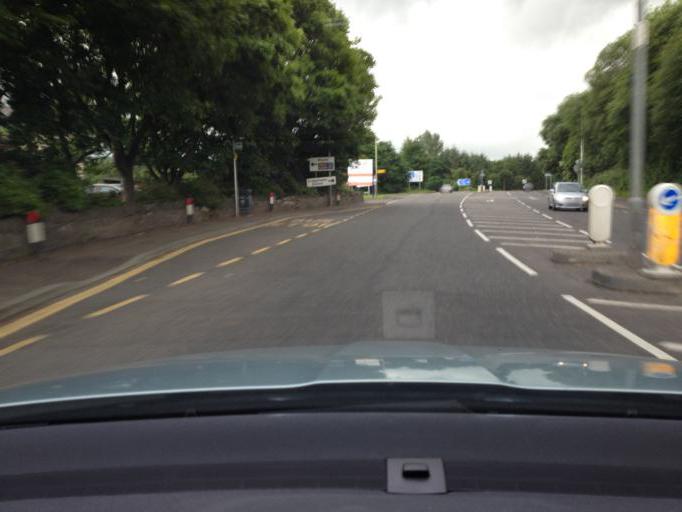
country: GB
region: Scotland
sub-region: Perth and Kinross
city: Perth
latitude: 56.3736
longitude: -3.4243
